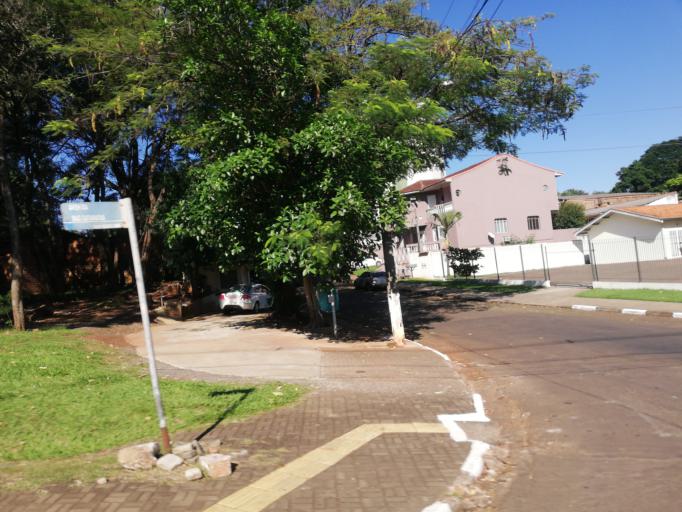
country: BR
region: Parana
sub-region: Foz Do Iguacu
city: Foz do Iguacu
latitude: -25.5490
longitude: -54.5757
